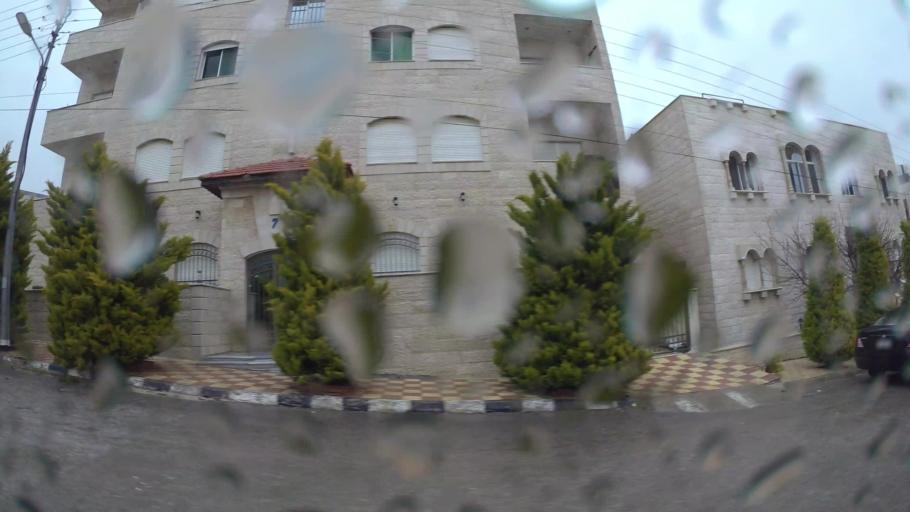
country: JO
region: Amman
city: Al Jubayhah
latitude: 32.0499
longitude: 35.8805
